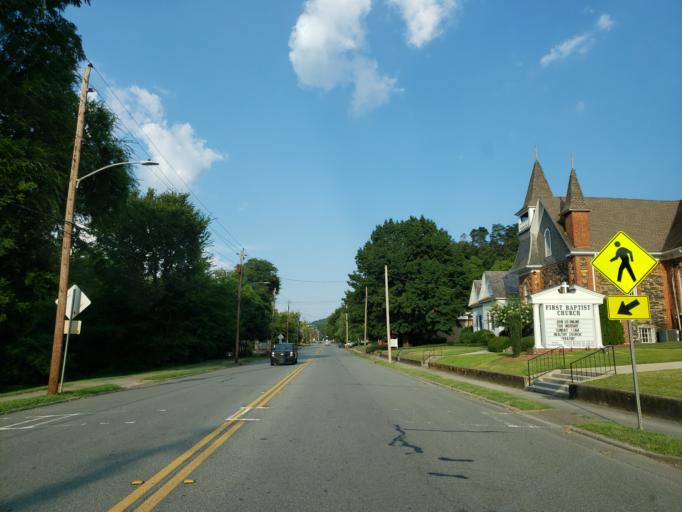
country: US
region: Georgia
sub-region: Polk County
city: Rockmart
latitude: 33.9966
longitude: -85.0486
